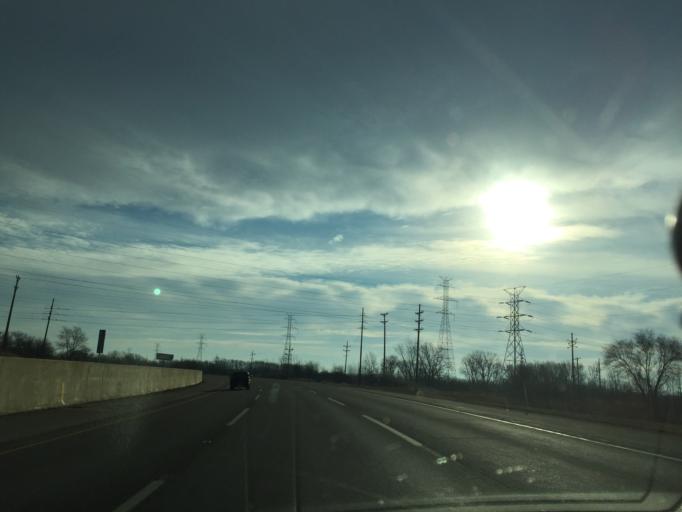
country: US
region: Indiana
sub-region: Lake County
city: New Chicago
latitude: 41.5855
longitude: -87.2997
